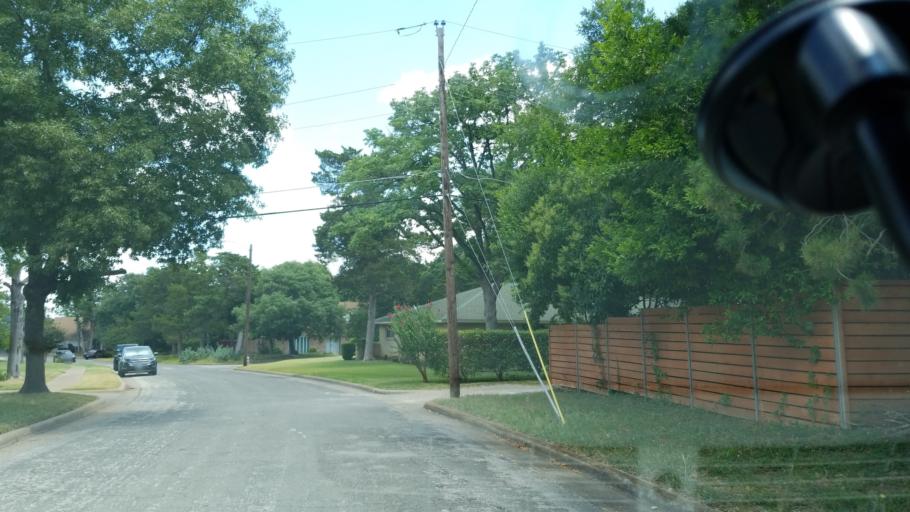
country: US
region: Texas
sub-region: Dallas County
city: Cockrell Hill
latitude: 32.6959
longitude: -96.8485
